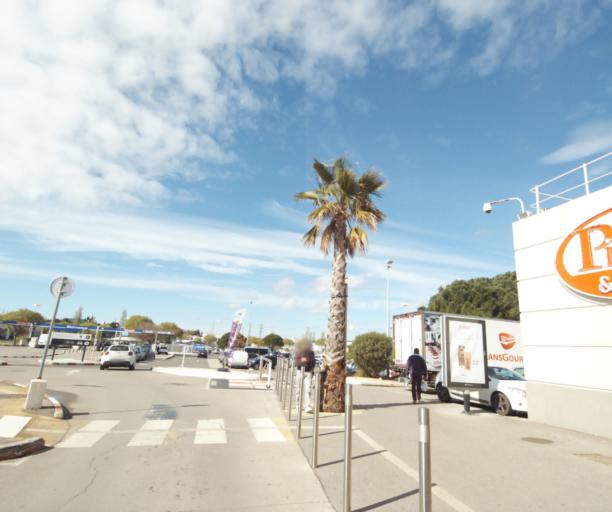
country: FR
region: Languedoc-Roussillon
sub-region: Departement de l'Herault
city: Saint-Jean-de-Vedas
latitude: 43.5715
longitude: 3.8471
